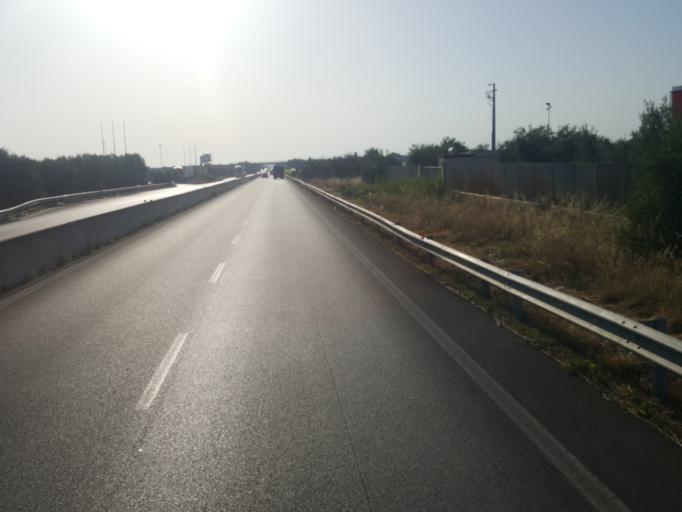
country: IT
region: Apulia
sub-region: Provincia di Barletta - Andria - Trani
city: San Ferdinando di Puglia
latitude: 41.3111
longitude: 16.0821
